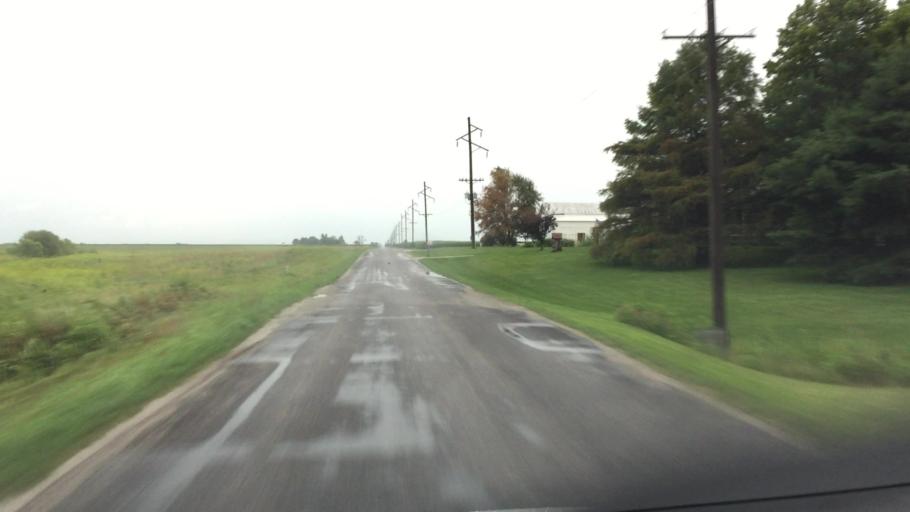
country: US
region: Iowa
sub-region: Lee County
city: Fort Madison
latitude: 40.5194
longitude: -91.2692
